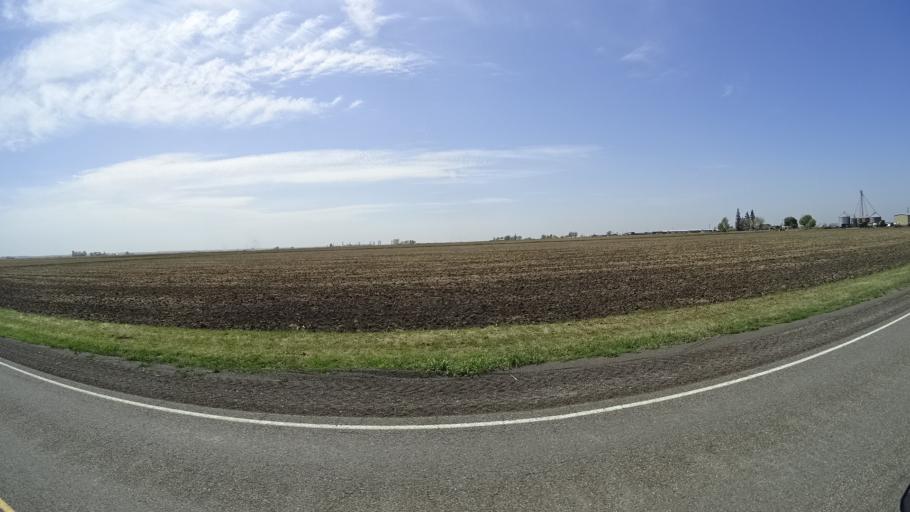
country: US
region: California
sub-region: Glenn County
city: Willows
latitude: 39.5828
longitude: -122.0613
